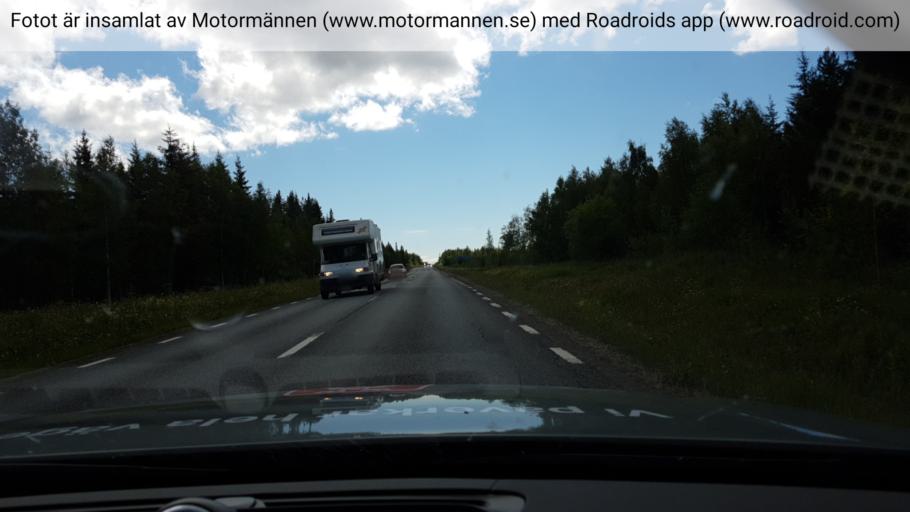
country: SE
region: Jaemtland
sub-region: Stroemsunds Kommun
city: Stroemsund
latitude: 63.7186
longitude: 15.4696
